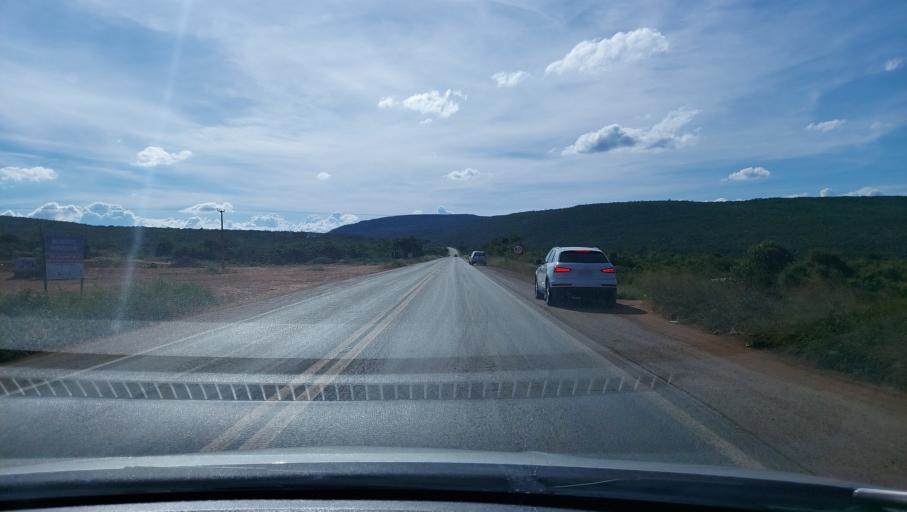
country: BR
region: Bahia
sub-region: Seabra
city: Seabra
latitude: -12.4574
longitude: -41.6476
